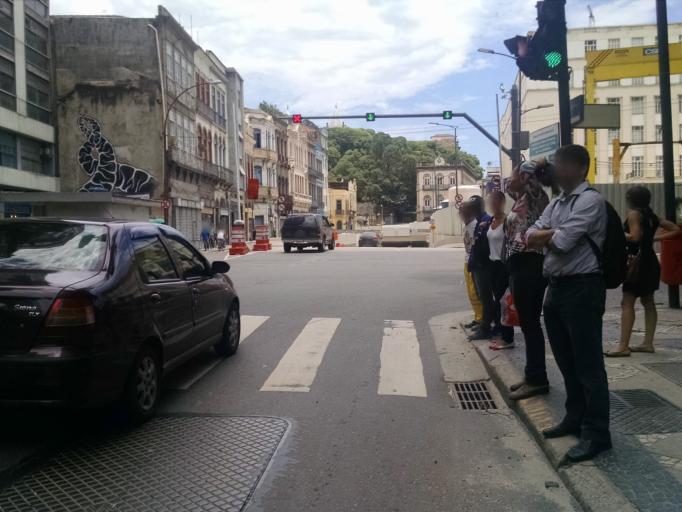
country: BR
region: Rio de Janeiro
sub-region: Rio De Janeiro
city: Rio de Janeiro
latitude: -22.8995
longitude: -43.1772
